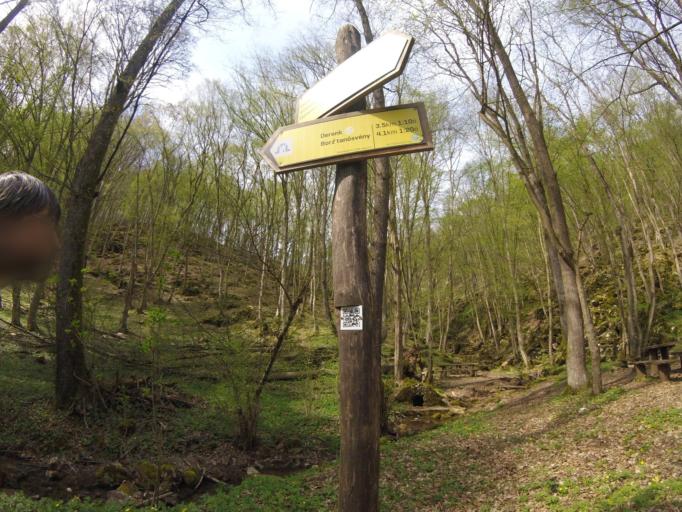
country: HU
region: Borsod-Abauj-Zemplen
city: Rudabanya
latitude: 48.5326
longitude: 20.6436
